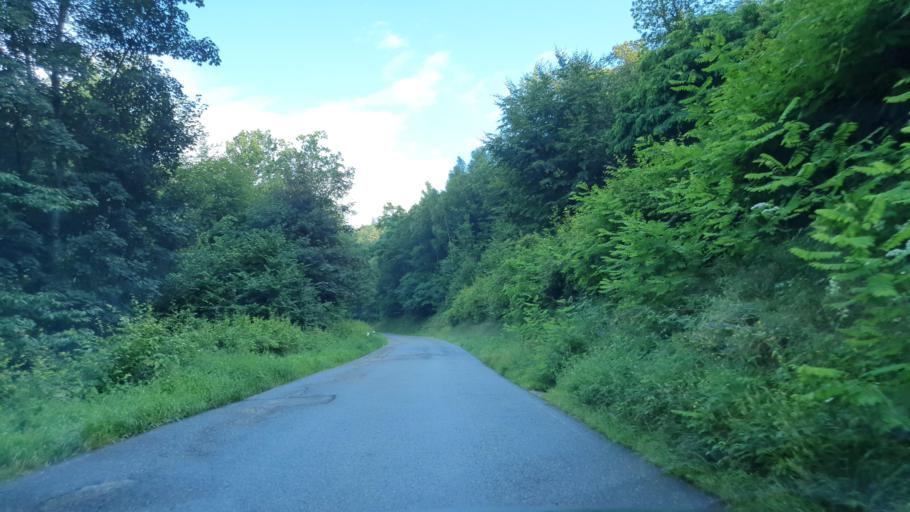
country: DE
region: Rheinland-Pfalz
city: Wernersberg
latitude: 49.1900
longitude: 7.9505
